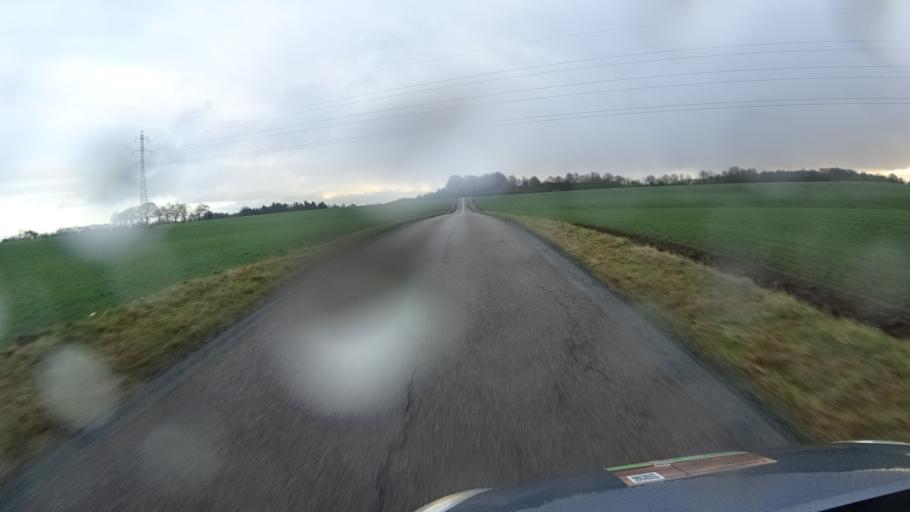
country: DK
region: South Denmark
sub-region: Vejle Kommune
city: Vejle
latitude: 55.7443
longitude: 9.5118
